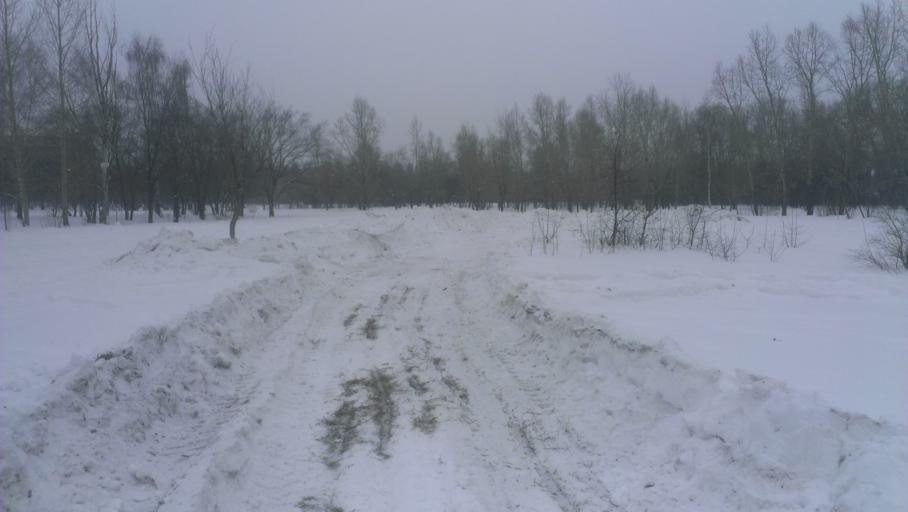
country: RU
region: Altai Krai
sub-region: Gorod Barnaulskiy
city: Barnaul
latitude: 53.3584
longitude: 83.6870
